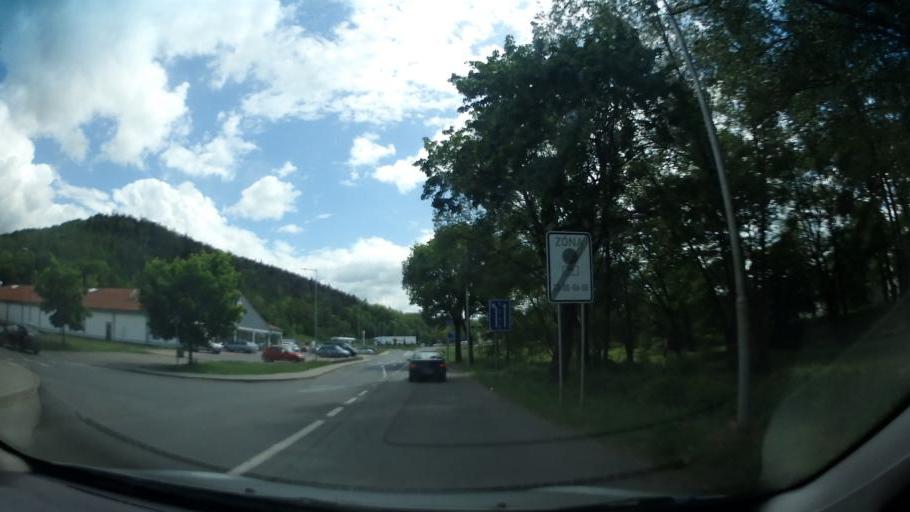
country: CZ
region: Pardubicky
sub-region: Okres Svitavy
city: Moravska Trebova
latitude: 49.7520
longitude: 16.6574
